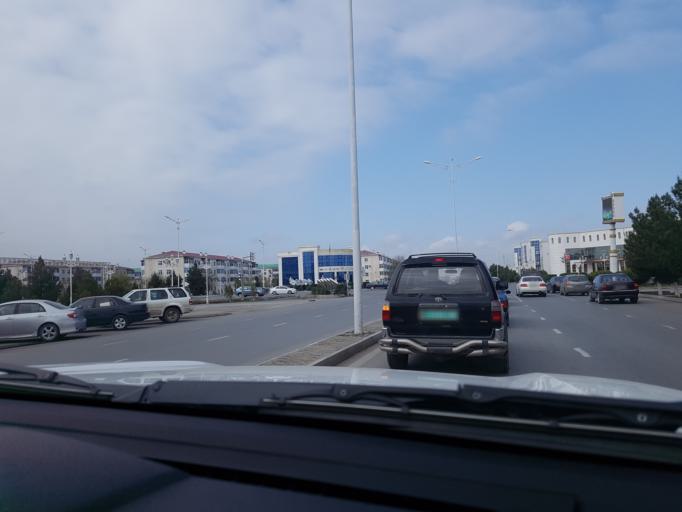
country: TM
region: Lebap
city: Turkmenabat
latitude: 39.0727
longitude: 63.5880
